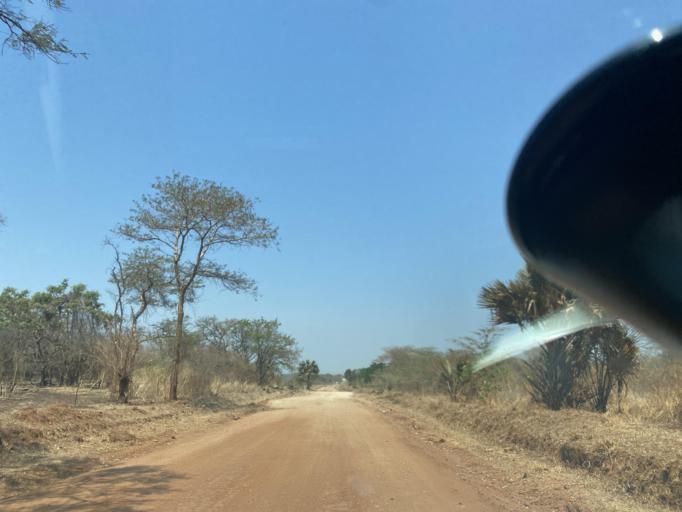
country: ZM
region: Lusaka
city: Lusaka
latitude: -15.5306
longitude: 28.0969
